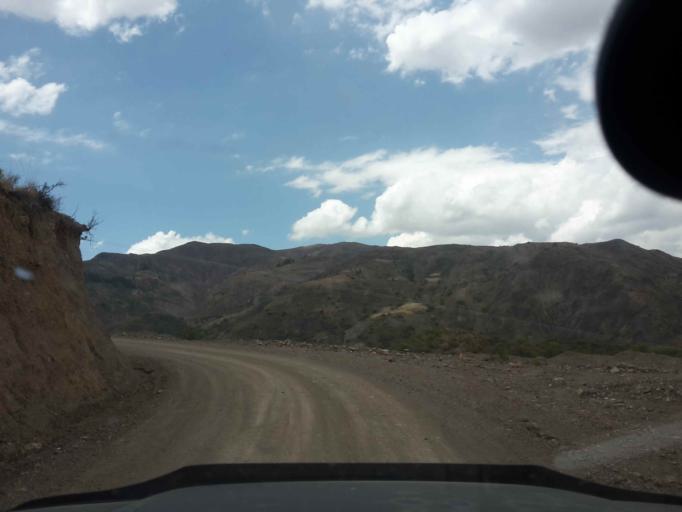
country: BO
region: Cochabamba
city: Sipe Sipe
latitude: -17.5230
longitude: -66.5589
